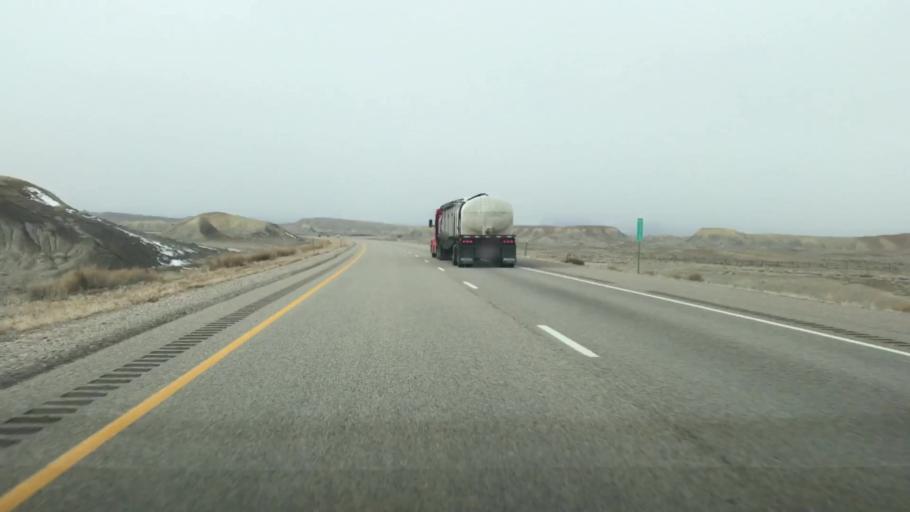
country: US
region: Utah
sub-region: Grand County
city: Moab
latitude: 38.9331
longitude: -110.0170
